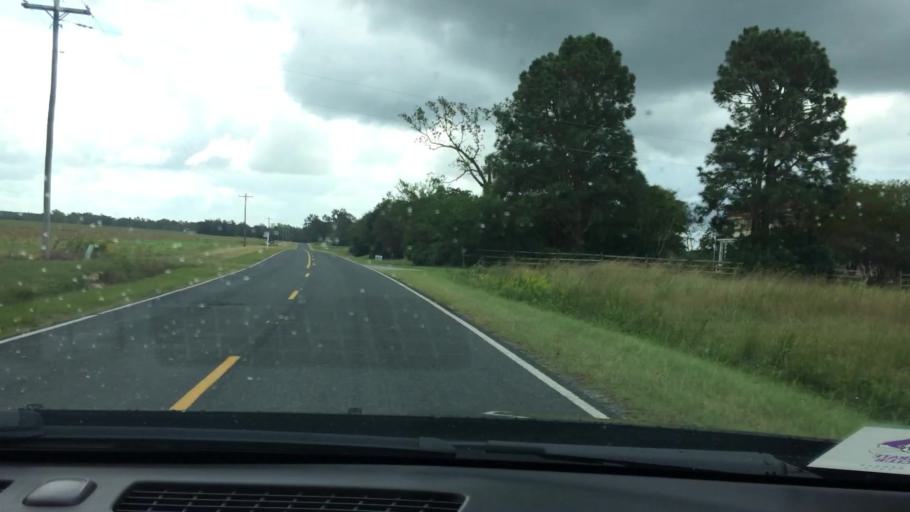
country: US
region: North Carolina
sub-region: Greene County
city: Maury
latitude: 35.5095
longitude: -77.5256
